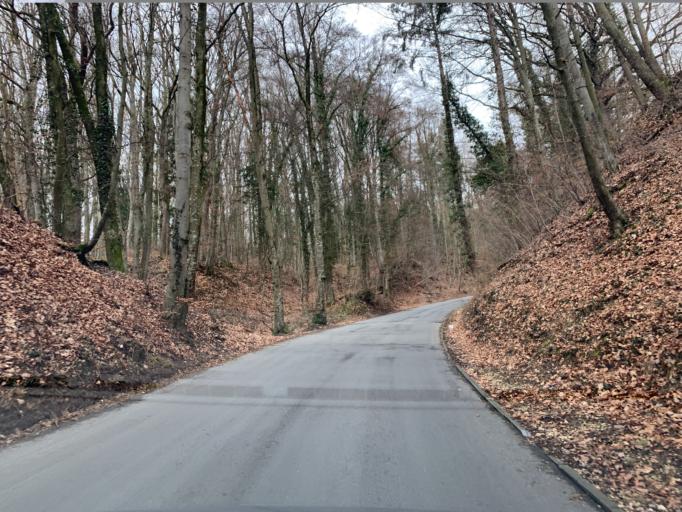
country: DE
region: Baden-Wuerttemberg
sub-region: Freiburg Region
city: Gailingen
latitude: 47.7022
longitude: 8.7508
